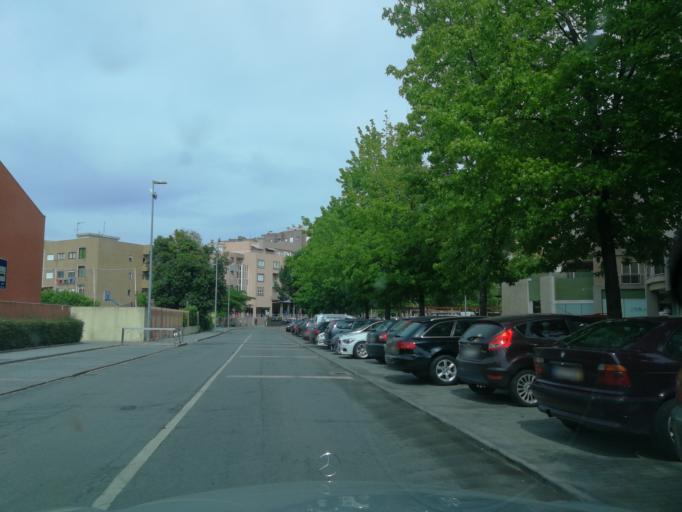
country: PT
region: Braga
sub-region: Vila Nova de Famalicao
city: Vila Nova de Famalicao
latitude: 41.4056
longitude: -8.5227
